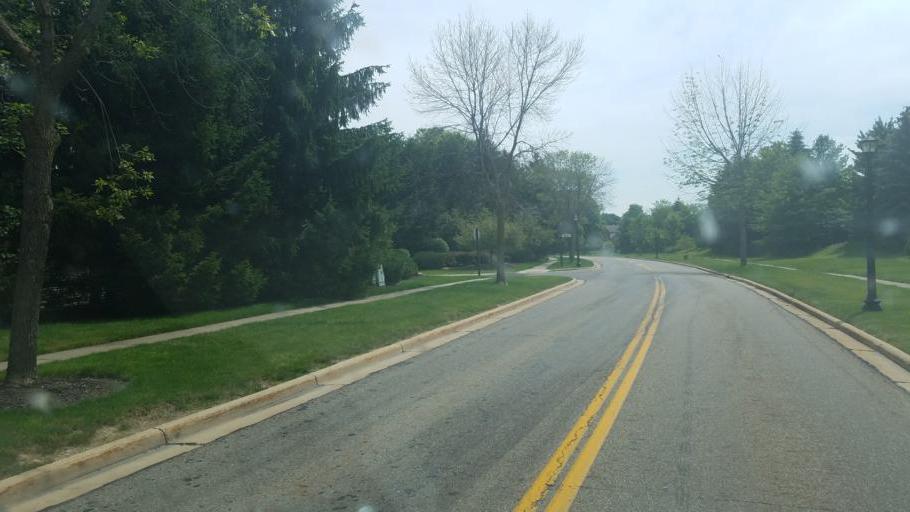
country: US
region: Ohio
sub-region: Summit County
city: Twinsburg
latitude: 41.3389
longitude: -81.4306
